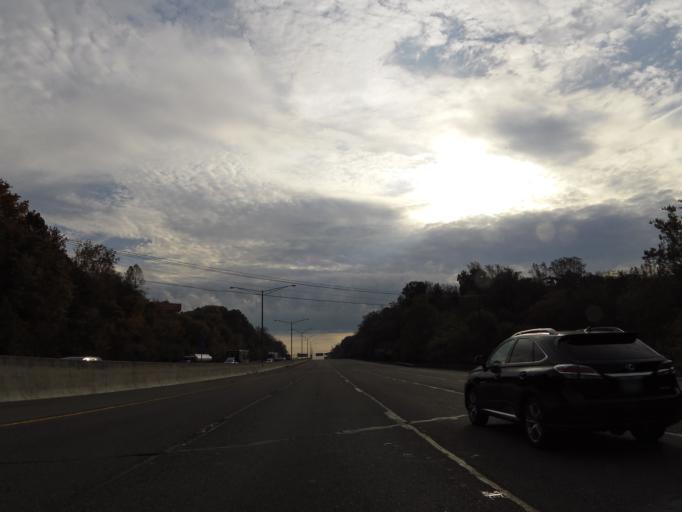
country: US
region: Tennessee
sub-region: Knox County
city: Knoxville
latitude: 36.0132
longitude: -83.8551
